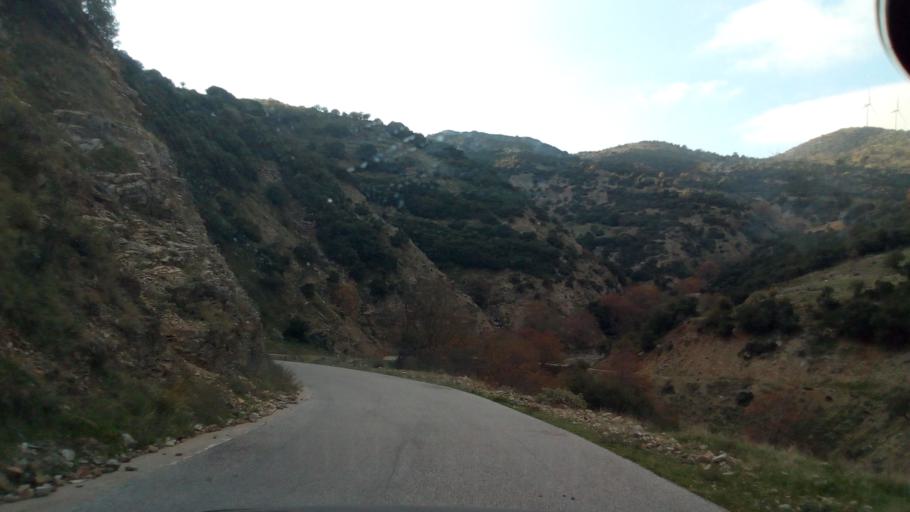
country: GR
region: West Greece
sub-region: Nomos Aitolias kai Akarnanias
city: Nafpaktos
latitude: 38.4239
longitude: 21.8170
